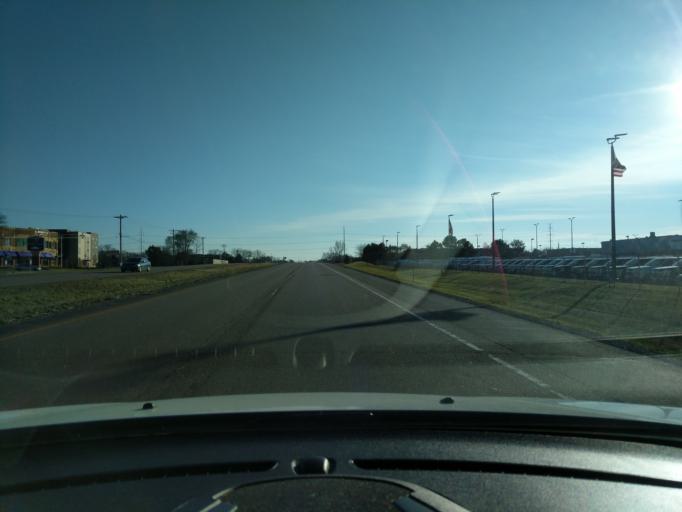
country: US
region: Minnesota
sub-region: Ramsey County
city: Roseville
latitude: 45.0252
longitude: -93.1672
